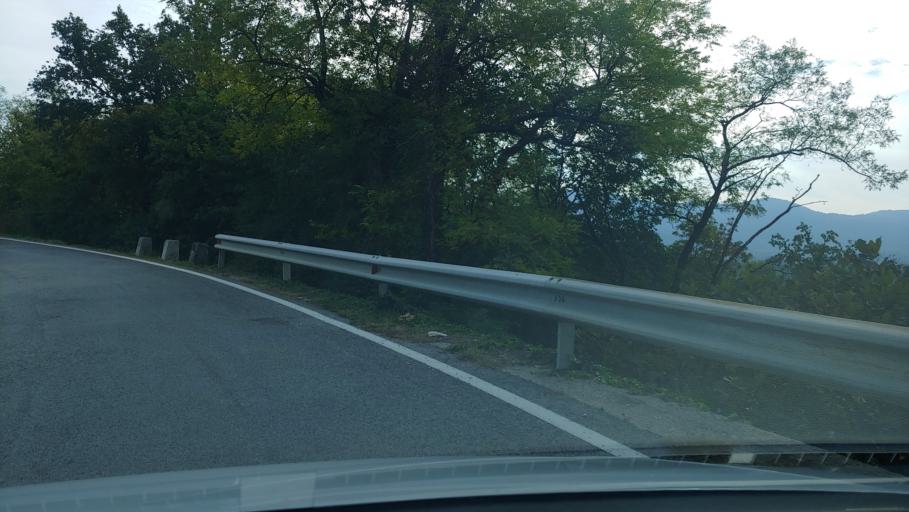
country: SI
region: Nova Gorica
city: Sempas
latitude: 45.9036
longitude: 13.7790
